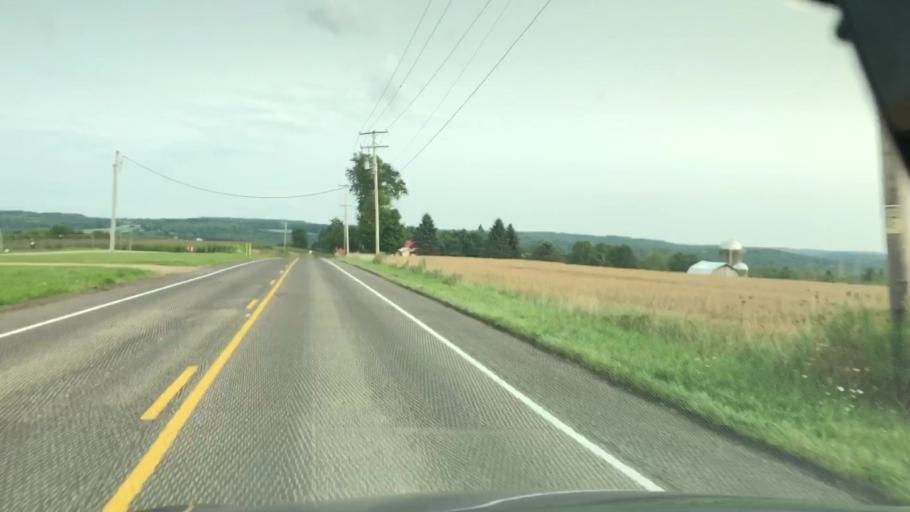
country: US
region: Pennsylvania
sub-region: Crawford County
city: Titusville
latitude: 41.7470
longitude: -79.7682
